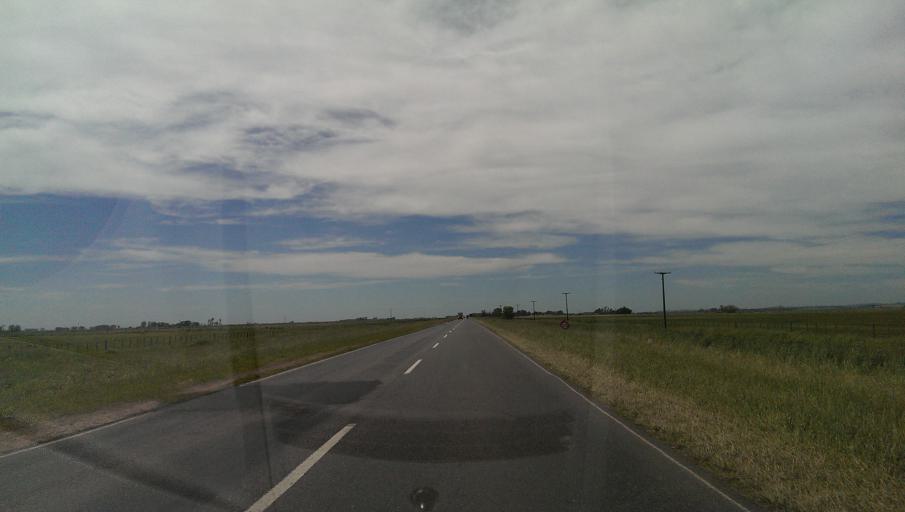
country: AR
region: Buenos Aires
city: Olavarria
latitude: -37.0461
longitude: -60.4424
